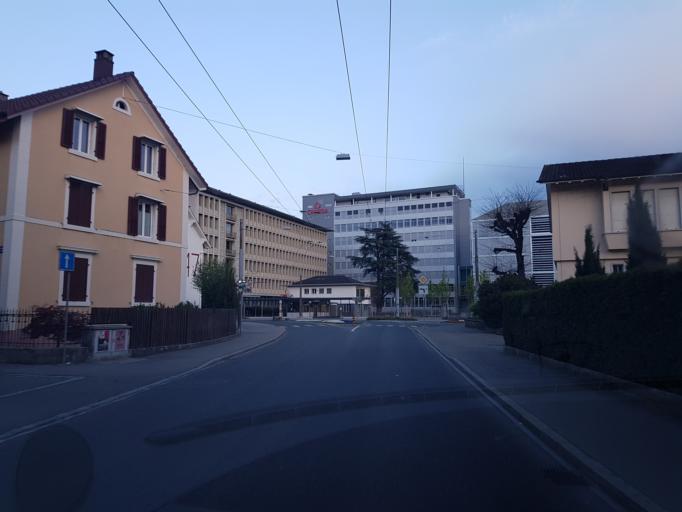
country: CH
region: Bern
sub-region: Biel/Bienne District
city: Biel/Bienne
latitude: 47.1443
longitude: 7.2582
